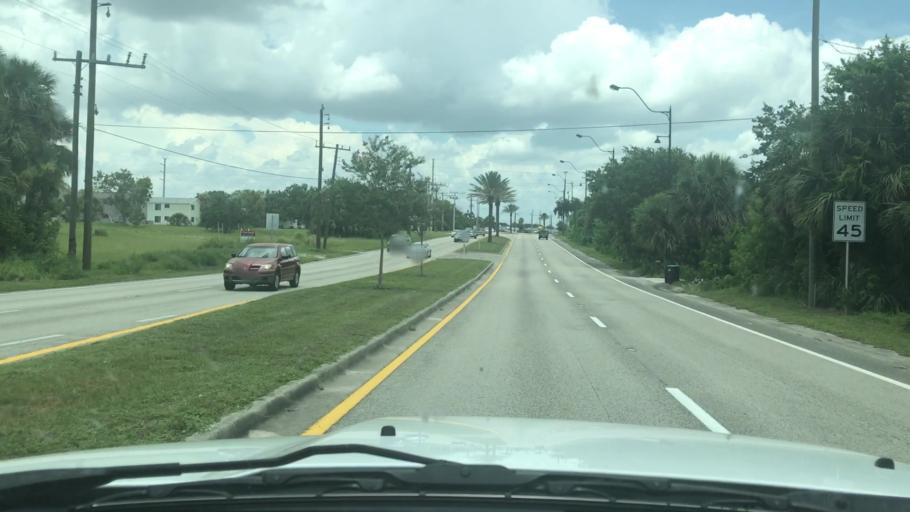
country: US
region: Florida
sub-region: Brevard County
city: Palm Bay
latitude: 28.0432
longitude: -80.5842
